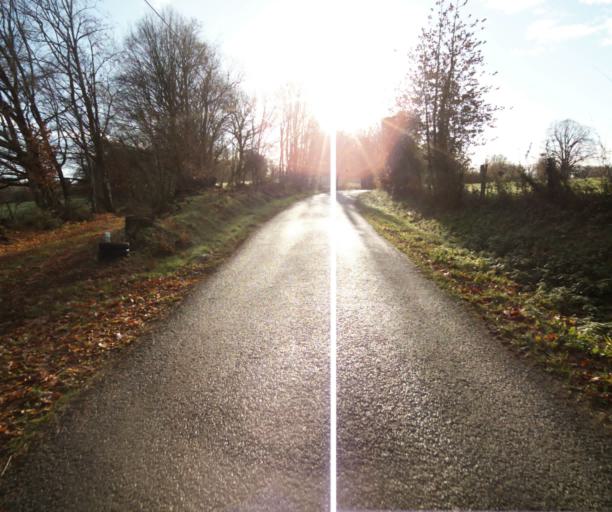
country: FR
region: Limousin
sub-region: Departement de la Correze
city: Sainte-Fereole
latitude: 45.2539
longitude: 1.6172
